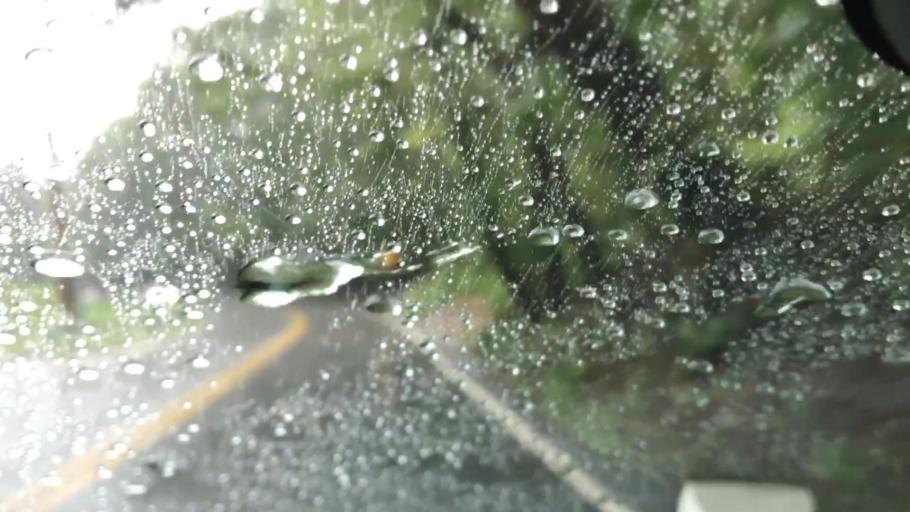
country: US
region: Pennsylvania
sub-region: Allegheny County
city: Glenshaw
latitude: 40.5299
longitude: -79.9821
